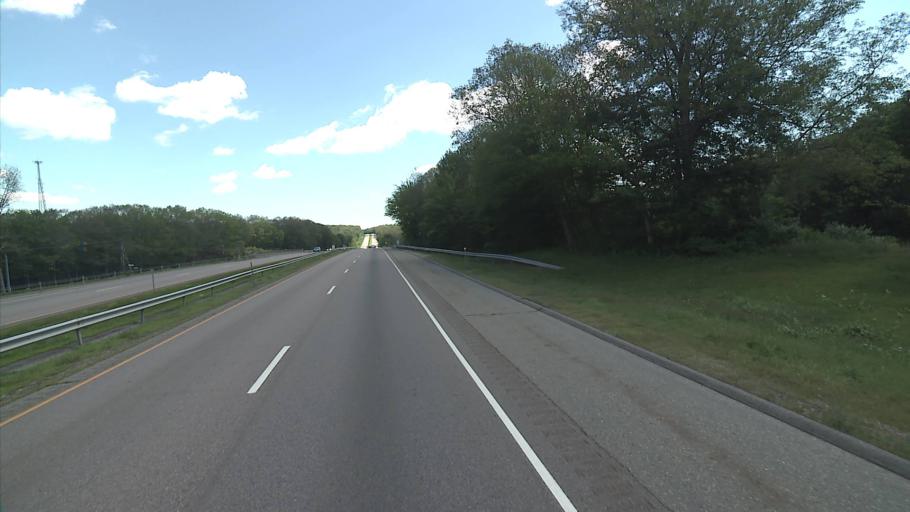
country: US
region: Connecticut
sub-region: New London County
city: Central Waterford
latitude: 41.3950
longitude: -72.1676
